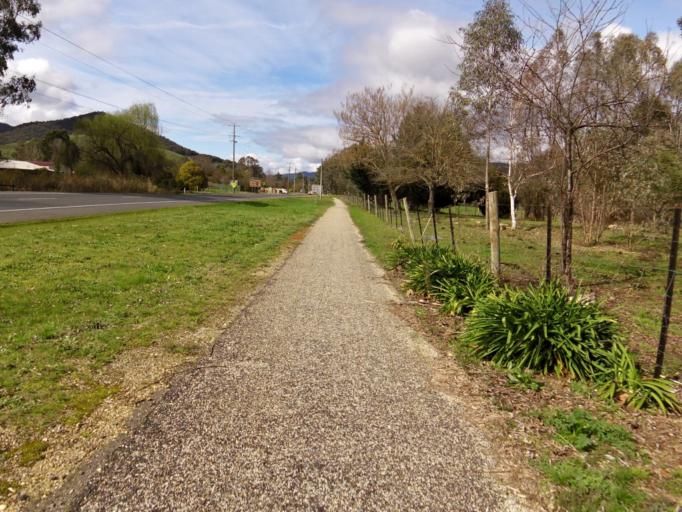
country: AU
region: Victoria
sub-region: Alpine
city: Mount Beauty
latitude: -36.5899
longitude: 146.7627
